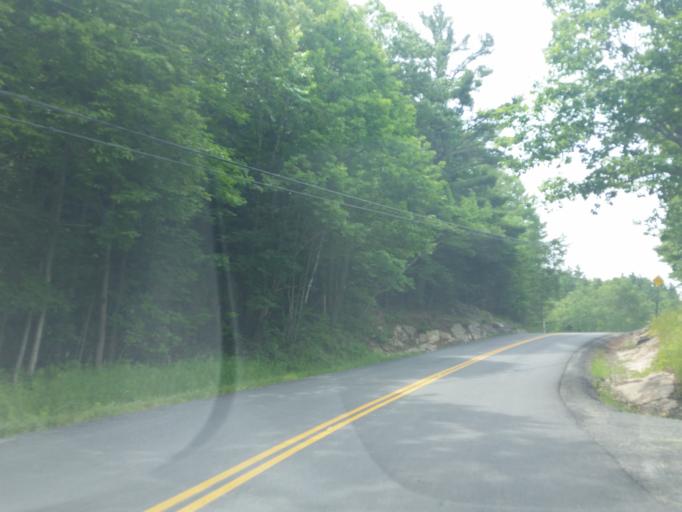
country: CA
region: Ontario
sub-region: Parry Sound District
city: Parry Sound
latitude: 45.3850
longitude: -80.0265
